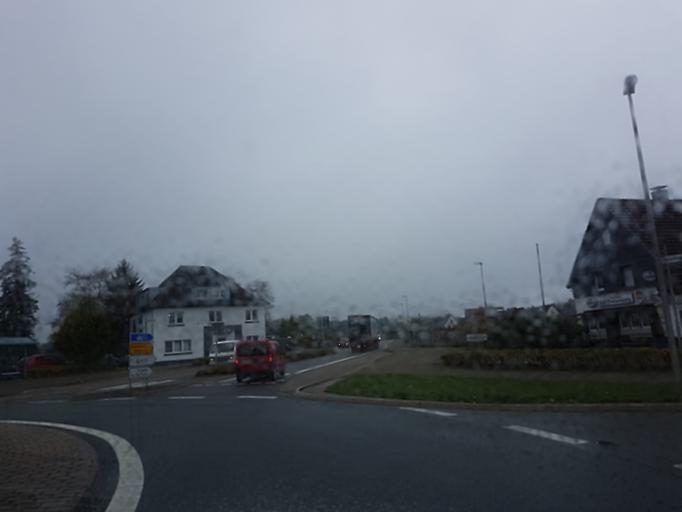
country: DE
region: North Rhine-Westphalia
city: Meinerzhagen
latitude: 51.0987
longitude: 7.6392
